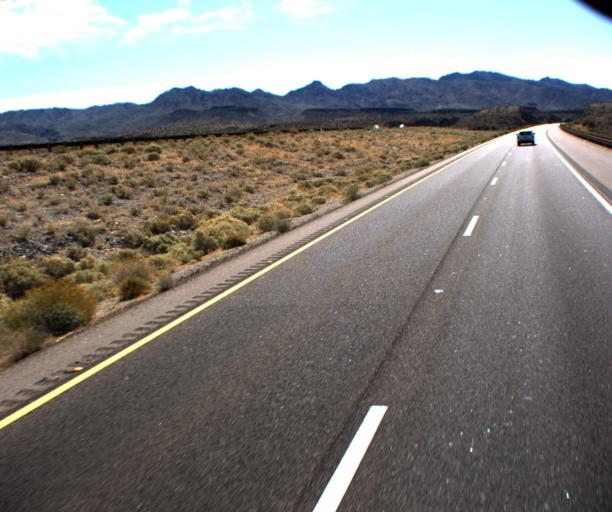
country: US
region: Nevada
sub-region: Clark County
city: Boulder City
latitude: 35.9539
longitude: -114.6535
